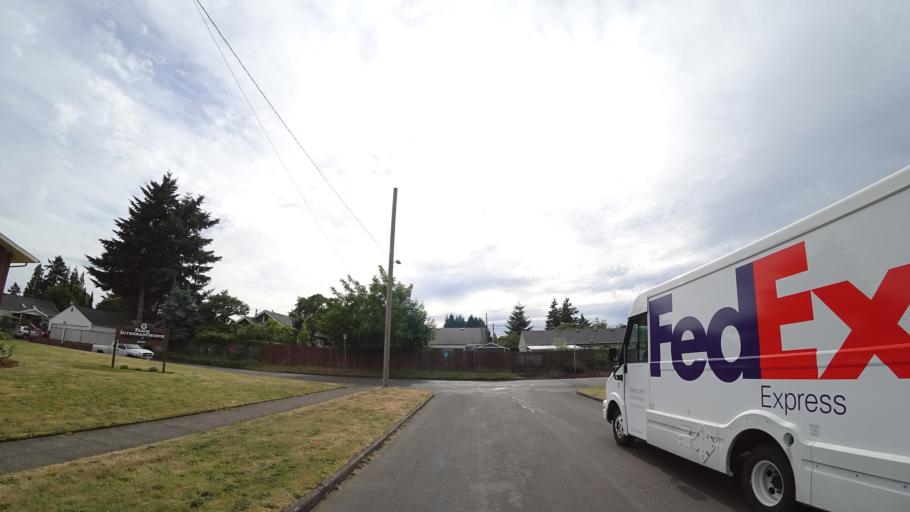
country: US
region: Oregon
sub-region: Multnomah County
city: Portland
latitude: 45.5708
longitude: -122.6895
